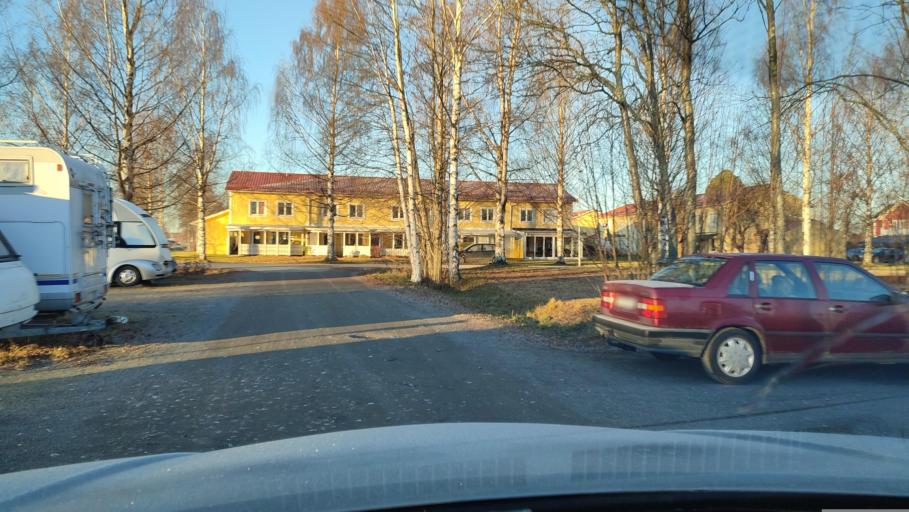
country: SE
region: Vaesterbotten
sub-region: Skelleftea Kommun
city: Skelleftea
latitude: 64.7452
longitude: 20.9839
